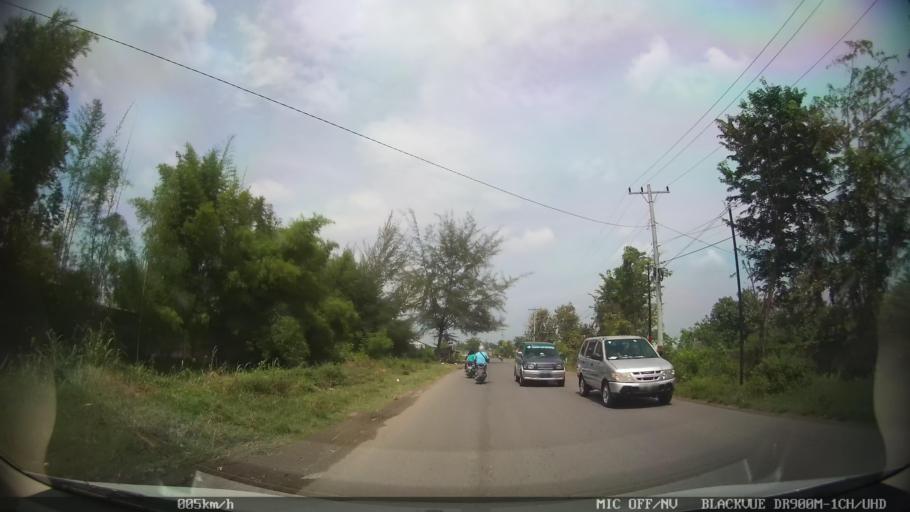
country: ID
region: North Sumatra
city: Medan
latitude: 3.6505
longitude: 98.7155
